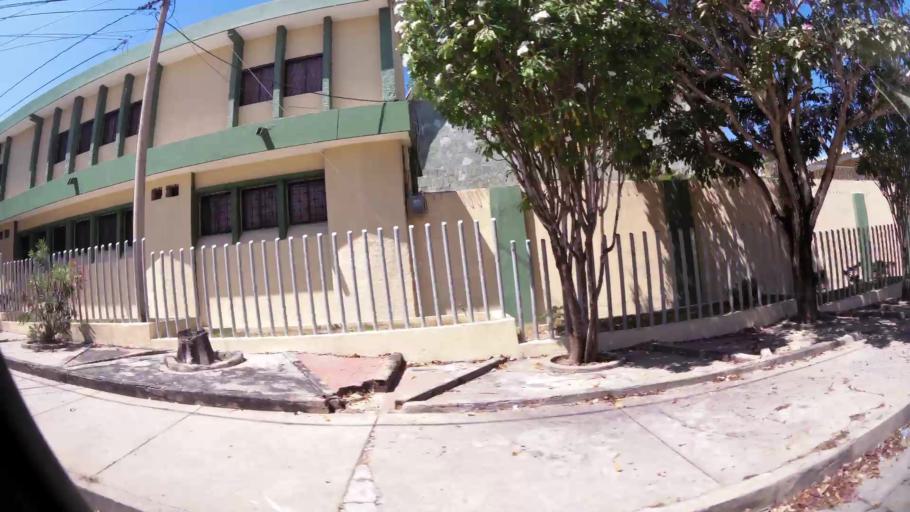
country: CO
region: Atlantico
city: Barranquilla
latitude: 10.9890
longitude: -74.8105
